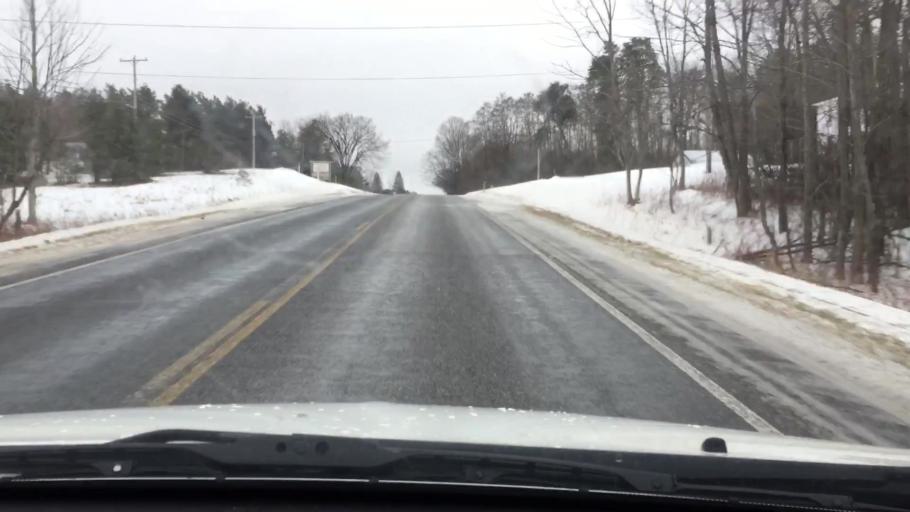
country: US
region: Michigan
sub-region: Wexford County
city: Cadillac
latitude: 44.0849
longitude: -85.4442
